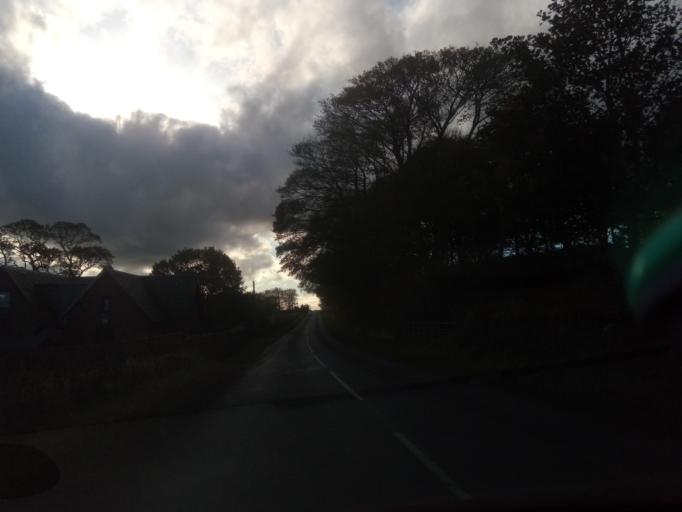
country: GB
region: Scotland
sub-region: The Scottish Borders
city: Chirnside
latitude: 55.8060
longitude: -2.1882
